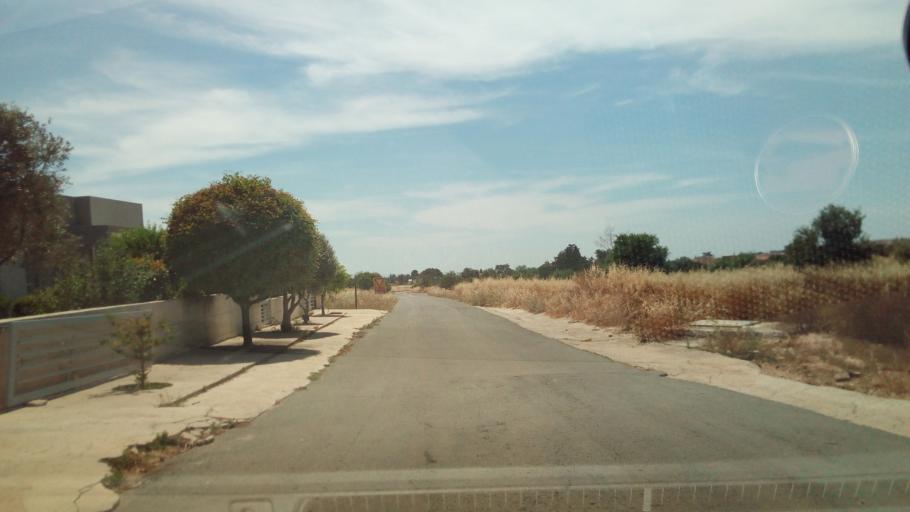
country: CY
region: Pafos
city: Mesogi
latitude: 34.7419
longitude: 32.5428
